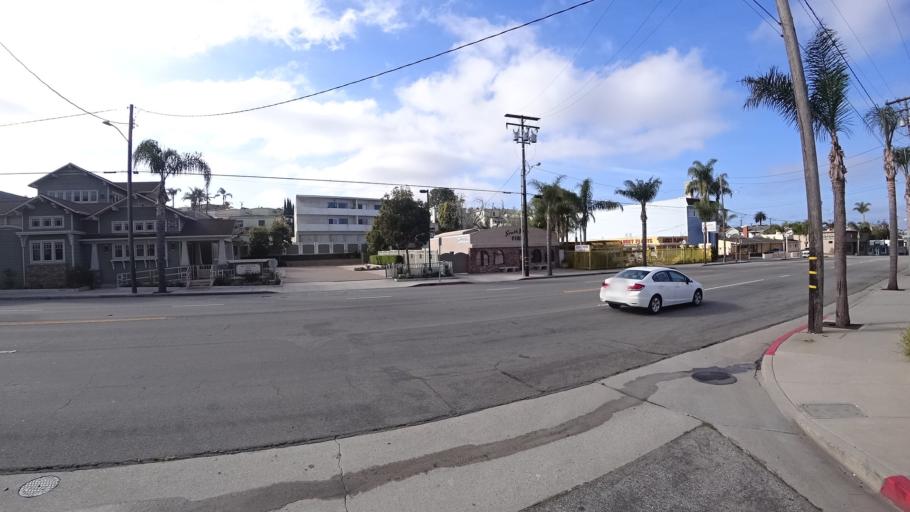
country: US
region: California
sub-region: Los Angeles County
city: Hermosa Beach
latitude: 33.8642
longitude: -118.3885
